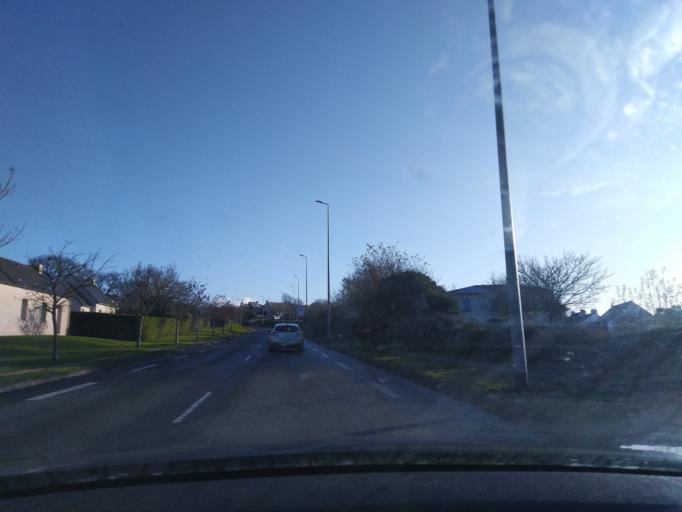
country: FR
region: Brittany
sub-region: Departement du Finistere
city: Morlaix
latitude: 48.5906
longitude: -3.8281
